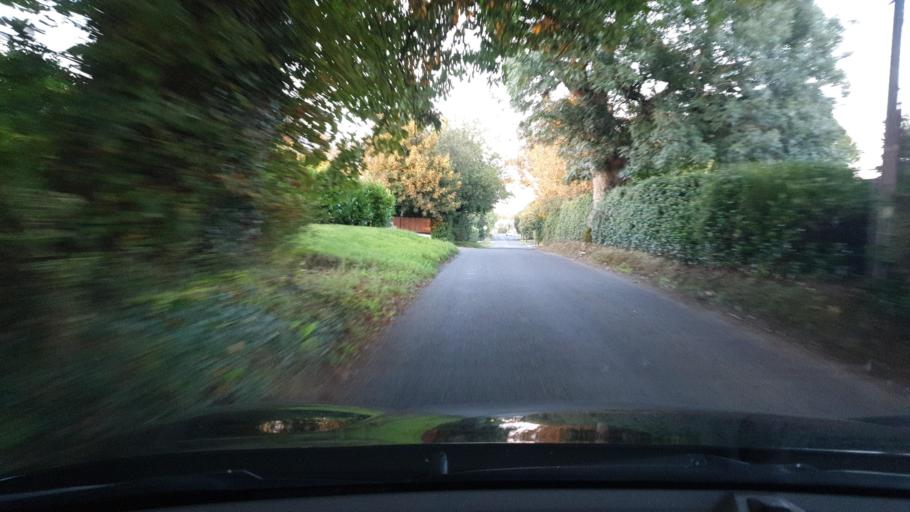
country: IE
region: Leinster
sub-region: Kildare
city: Prosperous
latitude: 53.3282
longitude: -6.7760
